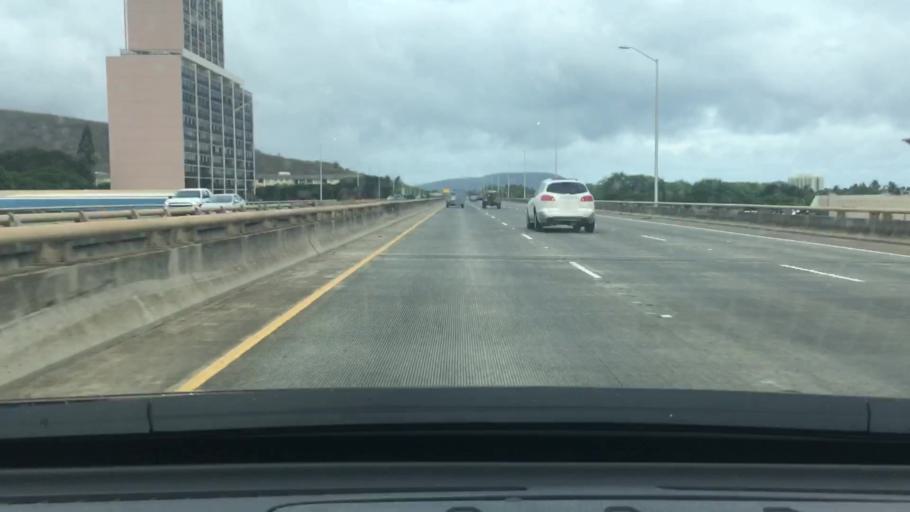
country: US
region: Hawaii
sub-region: Honolulu County
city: Honolulu
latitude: 21.2787
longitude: -157.7876
